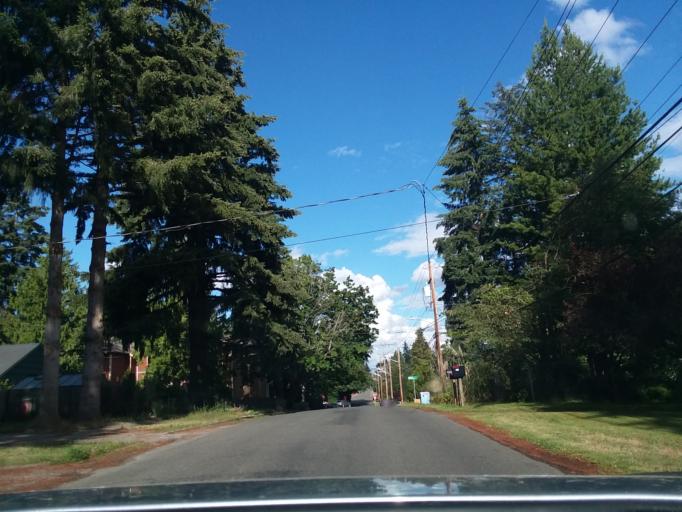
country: US
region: Washington
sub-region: King County
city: Shoreline
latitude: 47.7287
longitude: -122.3363
